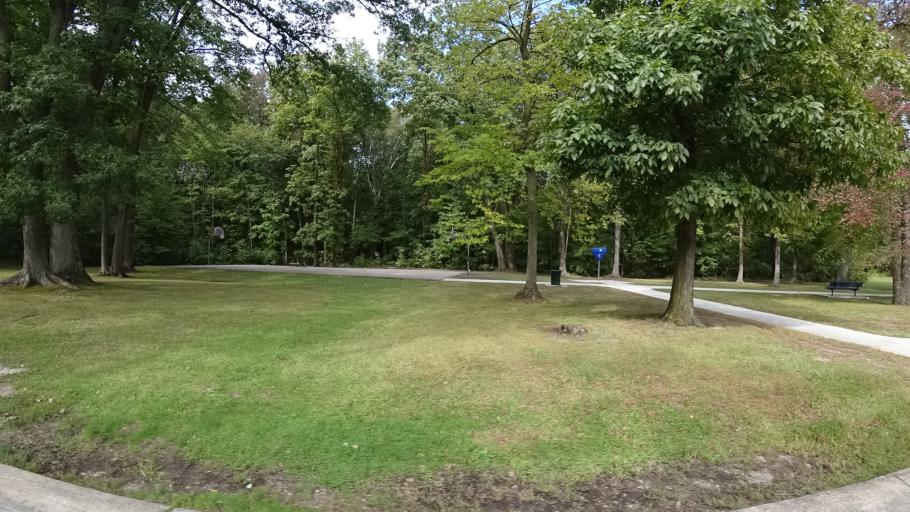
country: US
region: Indiana
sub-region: LaPorte County
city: Long Beach
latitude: 41.7176
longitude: -86.8344
